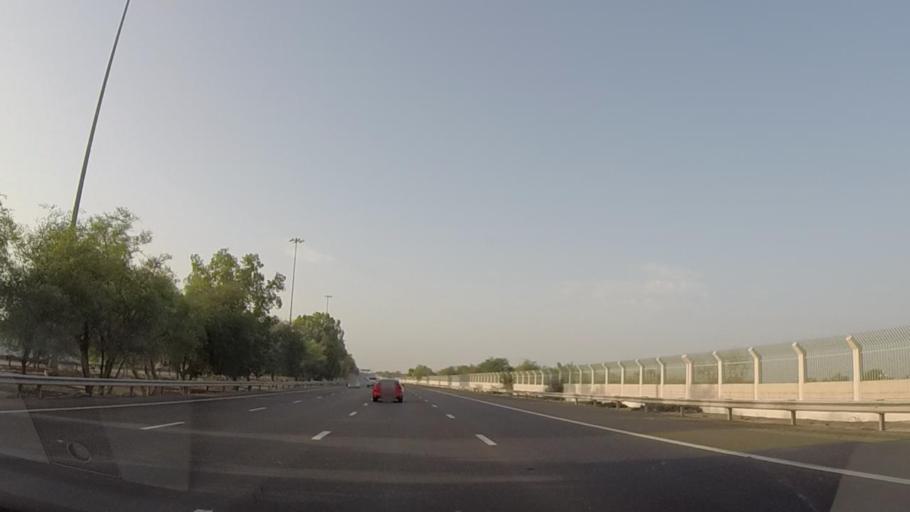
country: AE
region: Dubai
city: Dubai
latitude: 24.8133
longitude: 54.8706
